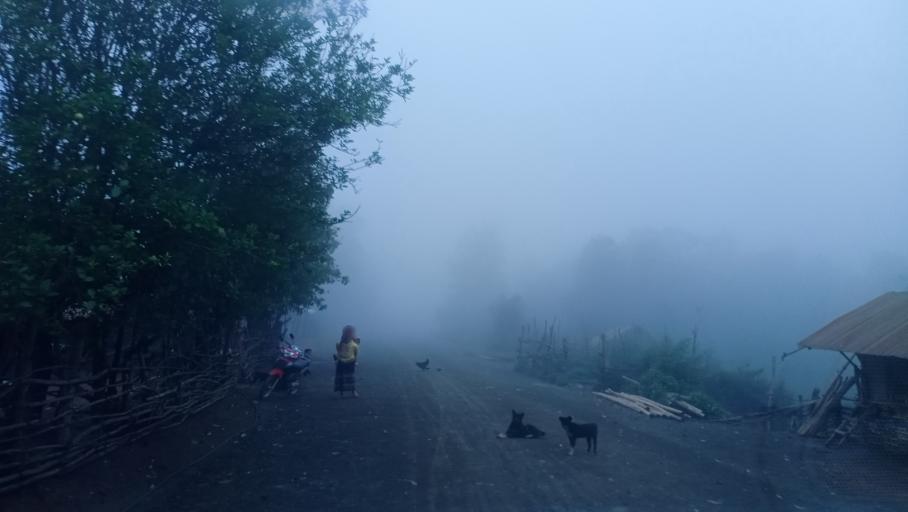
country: LA
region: Phongsali
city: Phongsali
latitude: 21.5056
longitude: 102.1727
